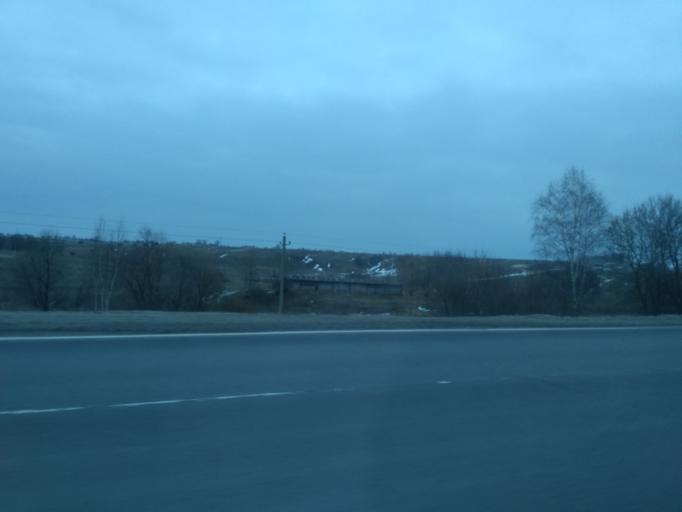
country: RU
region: Nizjnij Novgorod
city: Dal'neye Konstantinovo
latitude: 55.8038
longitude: 44.0107
